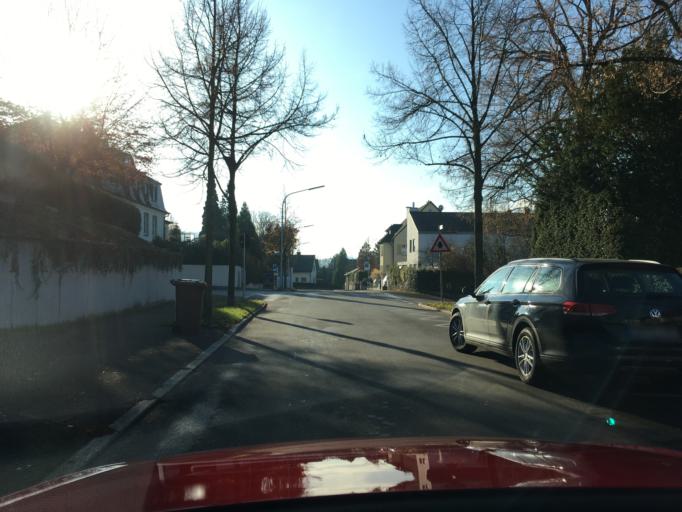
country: DE
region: Baden-Wuerttemberg
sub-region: Regierungsbezirk Stuttgart
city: Heilbronn
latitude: 49.1345
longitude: 9.2334
